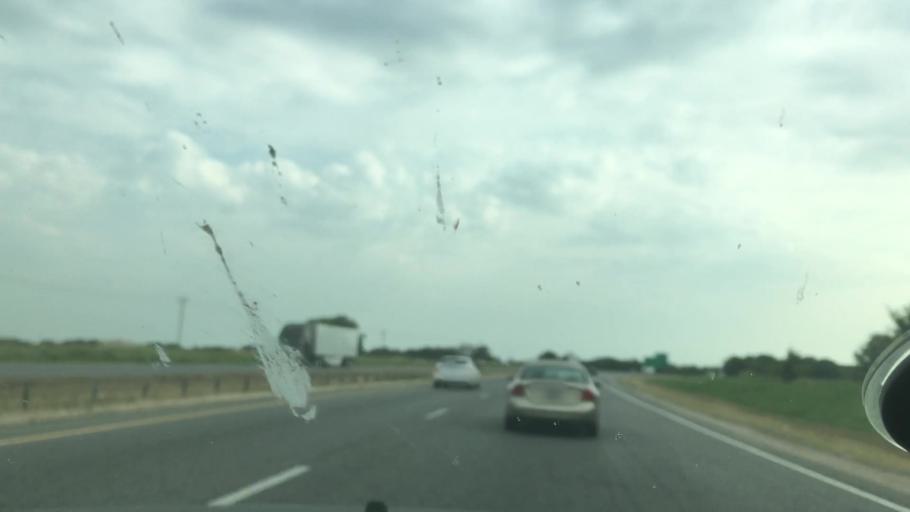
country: US
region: Oklahoma
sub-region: Bryan County
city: Colbert
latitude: 33.8671
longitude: -96.5111
